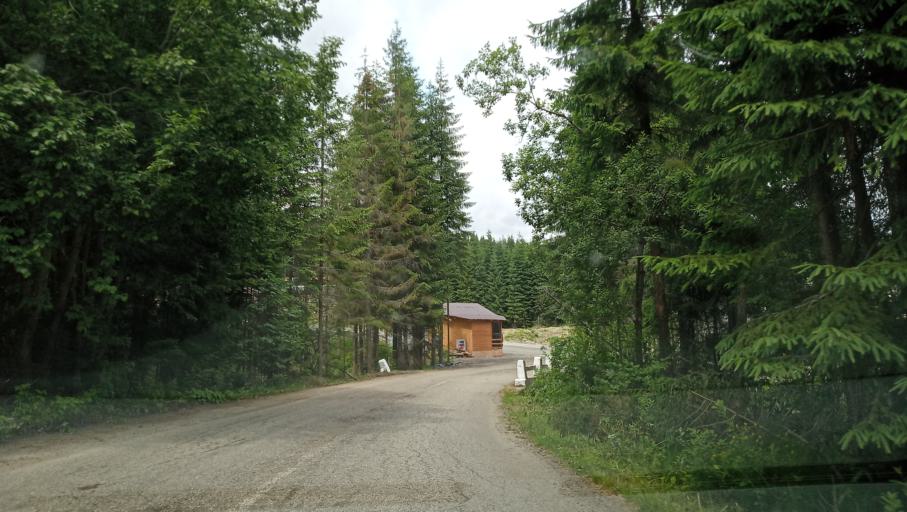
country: RO
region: Gorj
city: Novaci-Straini
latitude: 45.4166
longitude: 23.7076
